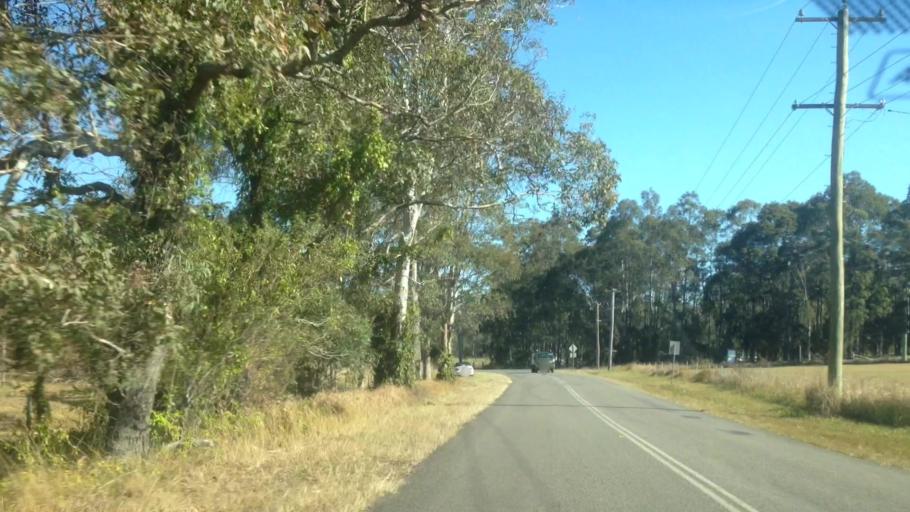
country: AU
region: New South Wales
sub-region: Lake Macquarie Shire
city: Cooranbong
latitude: -33.1154
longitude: 151.4469
